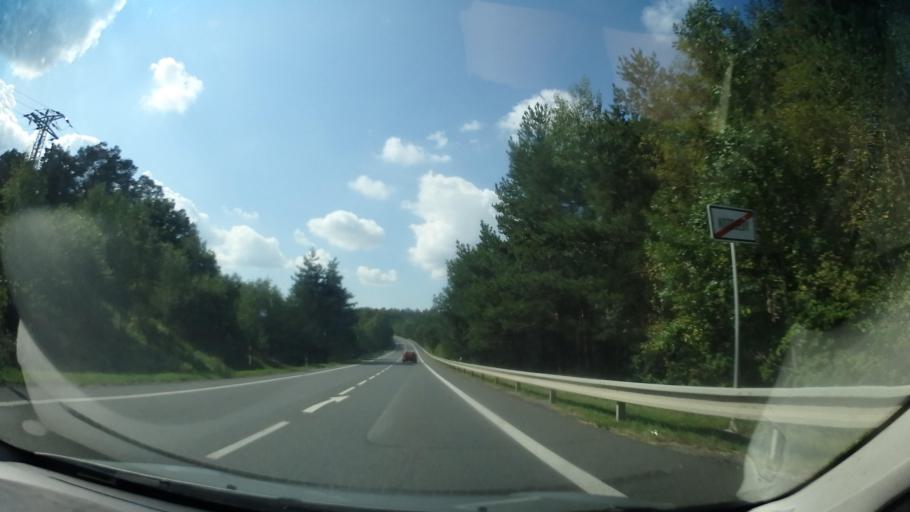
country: CZ
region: Central Bohemia
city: Kostelec nad Cernymi Lesy
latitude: 49.9916
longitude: 14.8092
